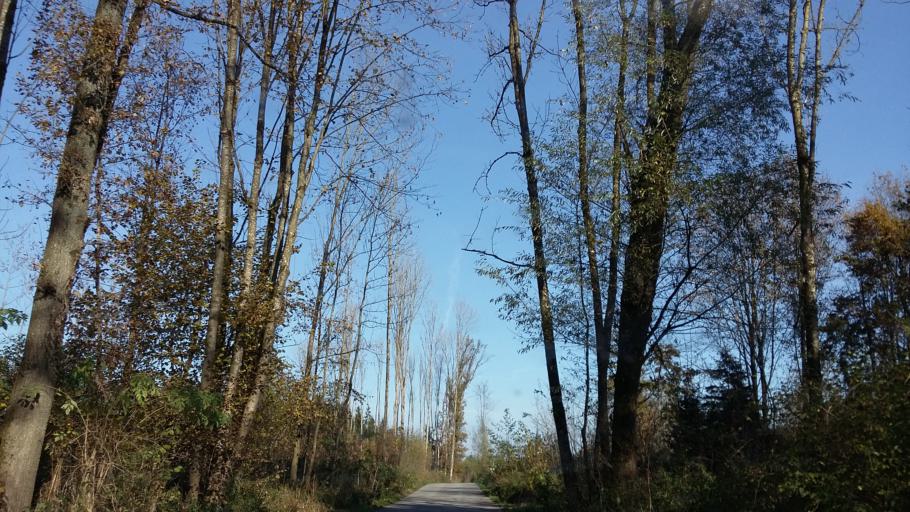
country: DE
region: Bavaria
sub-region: Upper Bavaria
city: Riedering
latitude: 47.8333
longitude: 12.1996
